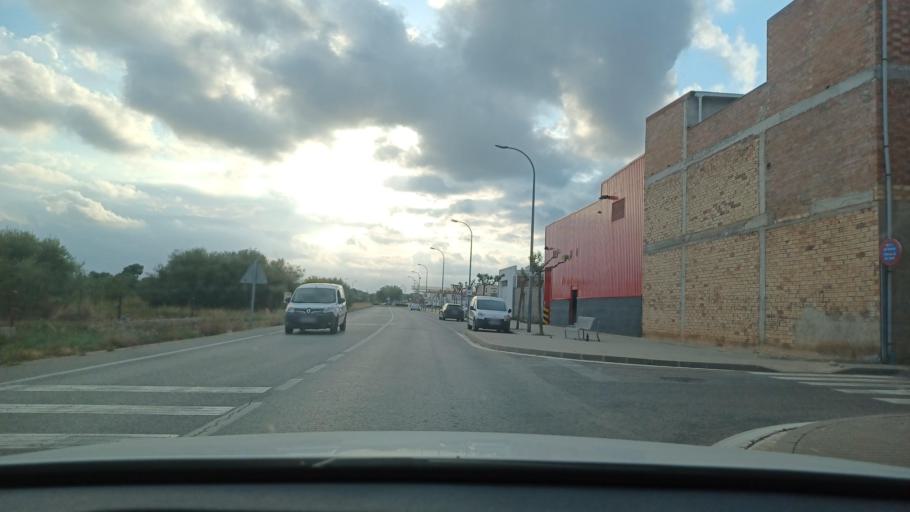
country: ES
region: Catalonia
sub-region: Provincia de Tarragona
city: Alcanar
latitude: 40.5394
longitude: 0.4813
